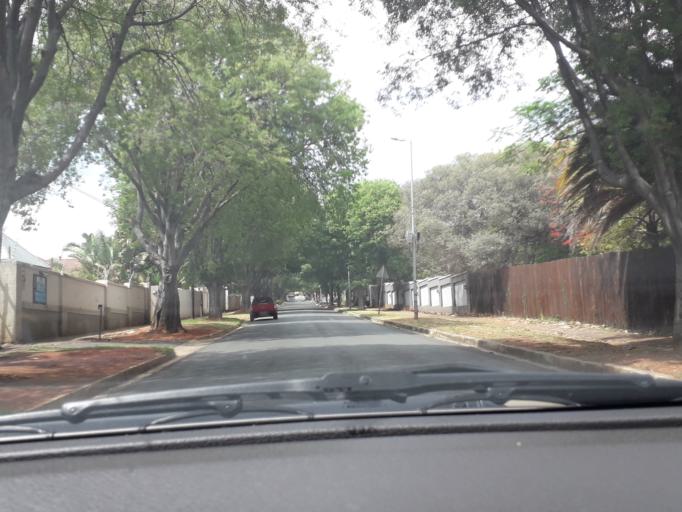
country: ZA
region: Gauteng
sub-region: City of Johannesburg Metropolitan Municipality
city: Johannesburg
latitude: -26.1360
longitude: 28.0851
